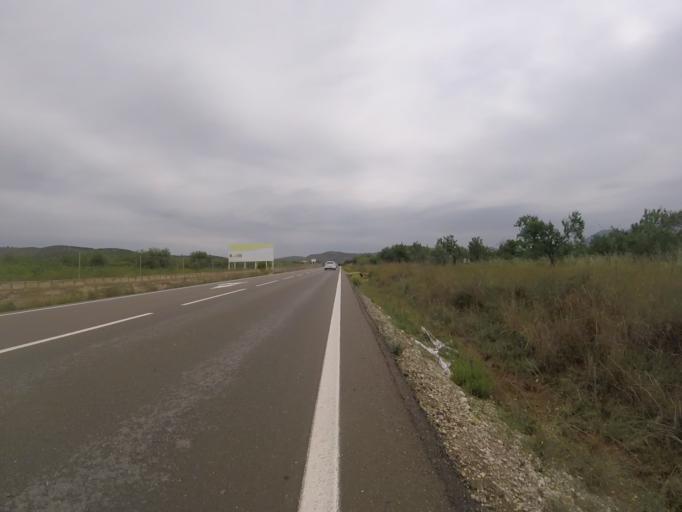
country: ES
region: Valencia
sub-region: Provincia de Castello
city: Alcoceber
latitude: 40.2581
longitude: 0.2443
